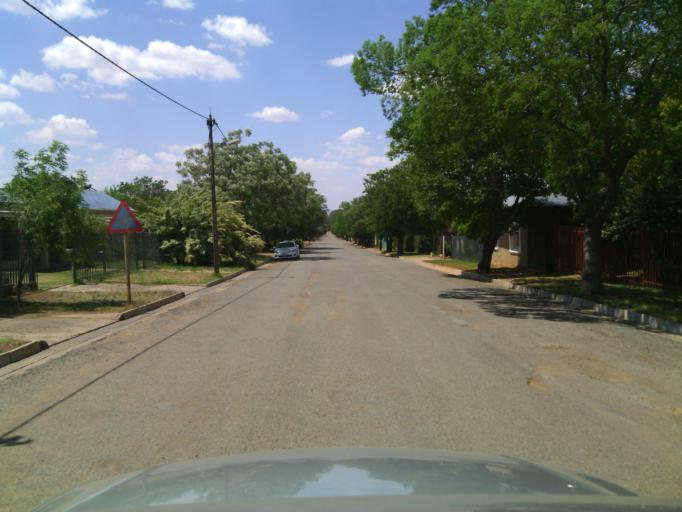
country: ZA
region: Orange Free State
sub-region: Xhariep District Municipality
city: Dewetsdorp
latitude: -29.5827
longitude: 26.6606
